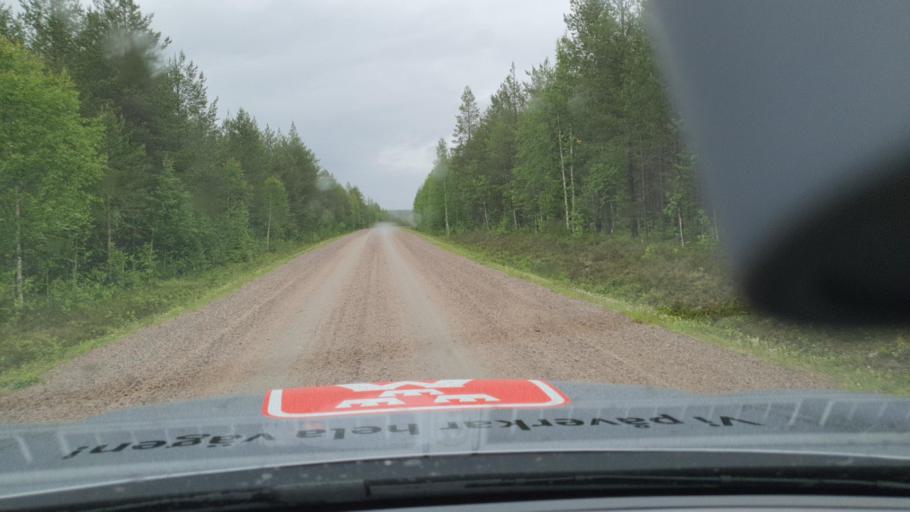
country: SE
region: Norrbotten
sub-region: Overkalix Kommun
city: OEverkalix
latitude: 66.5743
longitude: 22.7461
